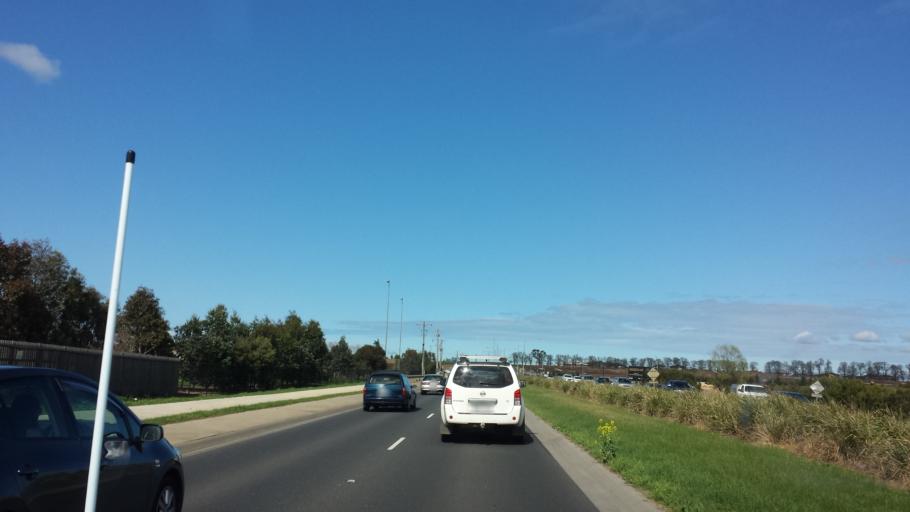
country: AU
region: Victoria
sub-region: Casey
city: Berwick
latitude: -38.0708
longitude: 145.3363
